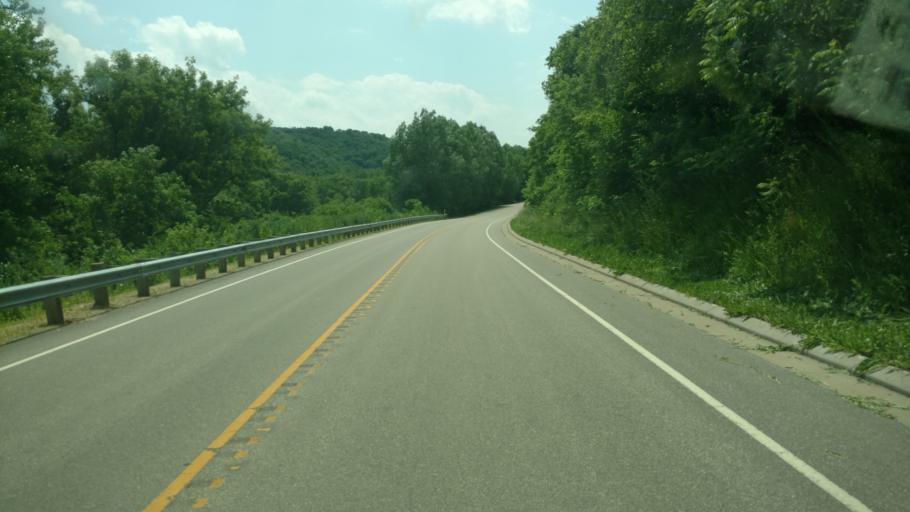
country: US
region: Wisconsin
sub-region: Vernon County
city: Viroqua
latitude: 43.4683
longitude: -90.7108
